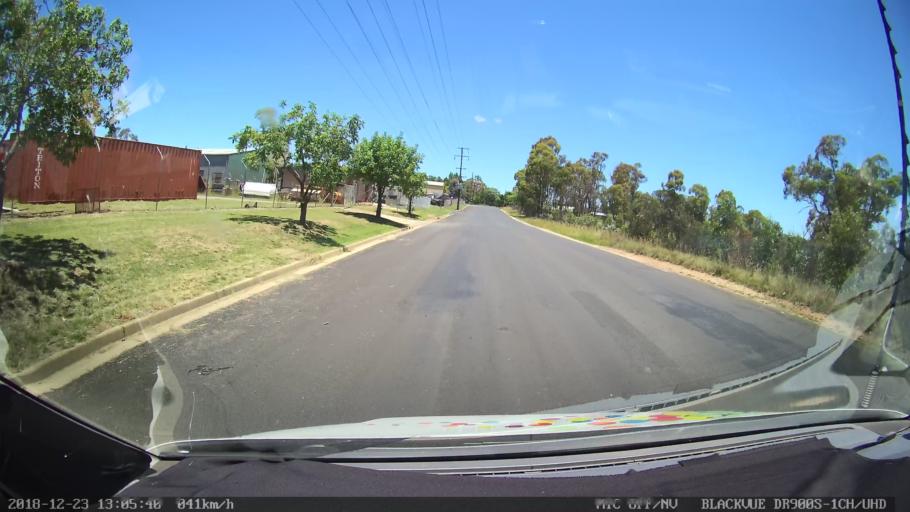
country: AU
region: New South Wales
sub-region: Armidale Dumaresq
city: Armidale
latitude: -30.5151
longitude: 151.6412
